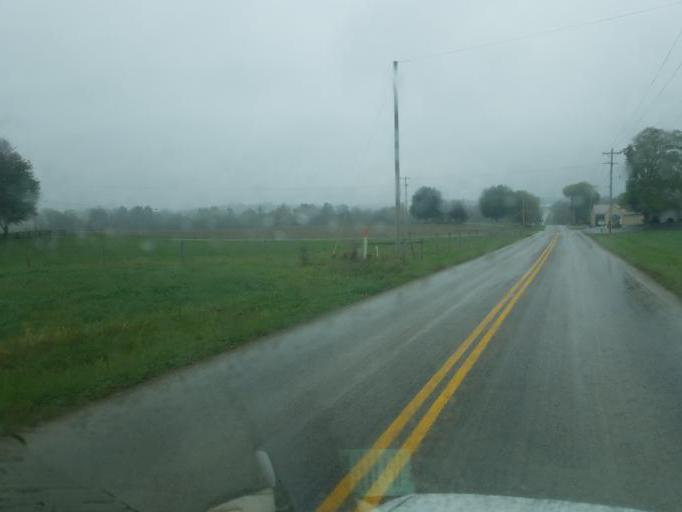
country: US
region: Ohio
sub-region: Wayne County
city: Shreve
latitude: 40.6289
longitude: -81.9945
